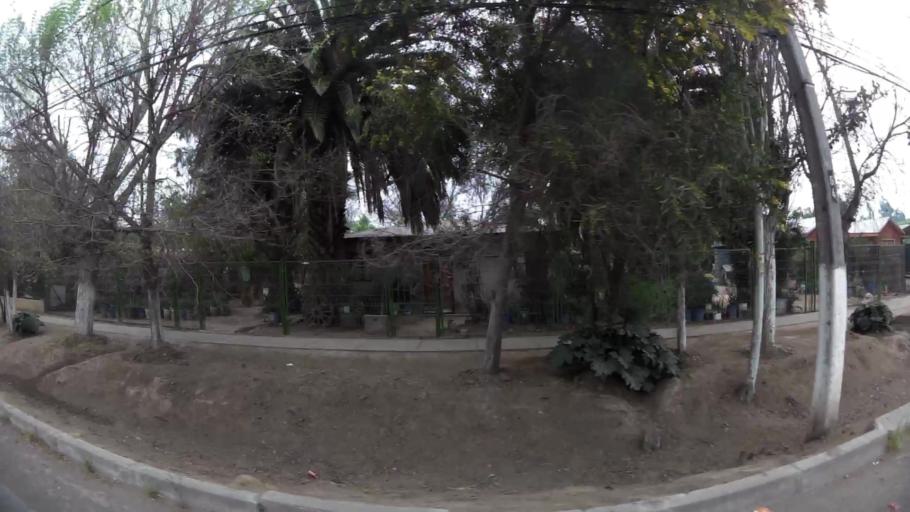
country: CL
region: Santiago Metropolitan
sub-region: Provincia de Chacabuco
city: Lampa
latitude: -33.2371
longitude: -70.8058
